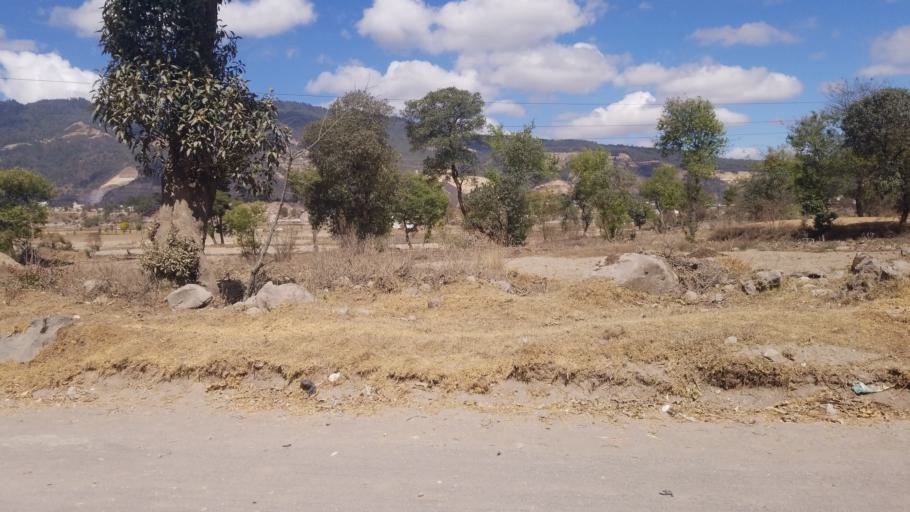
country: GT
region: Quetzaltenango
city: Quetzaltenango
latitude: 14.8044
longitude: -91.5364
